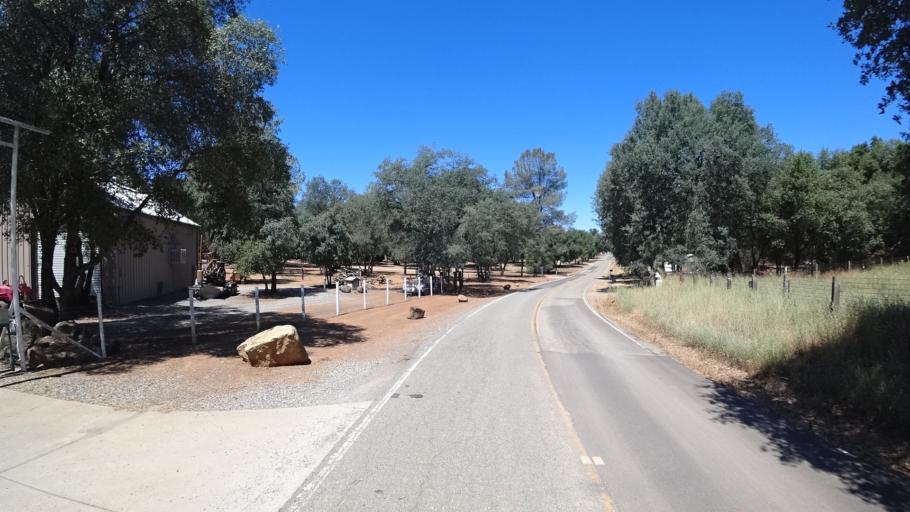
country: US
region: California
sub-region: Calaveras County
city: Mountain Ranch
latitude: 38.2095
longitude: -120.5261
